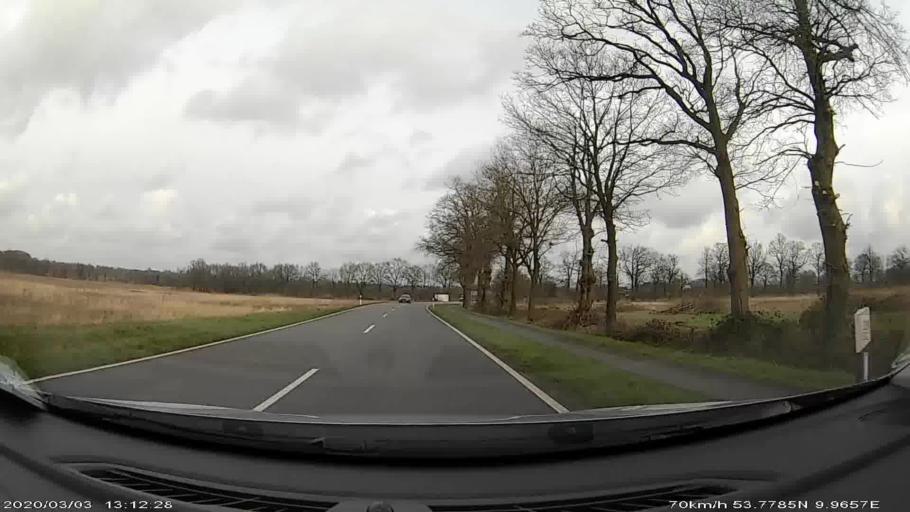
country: DE
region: Schleswig-Holstein
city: Henstedt-Ulzburg
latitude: 53.7794
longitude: 9.9676
